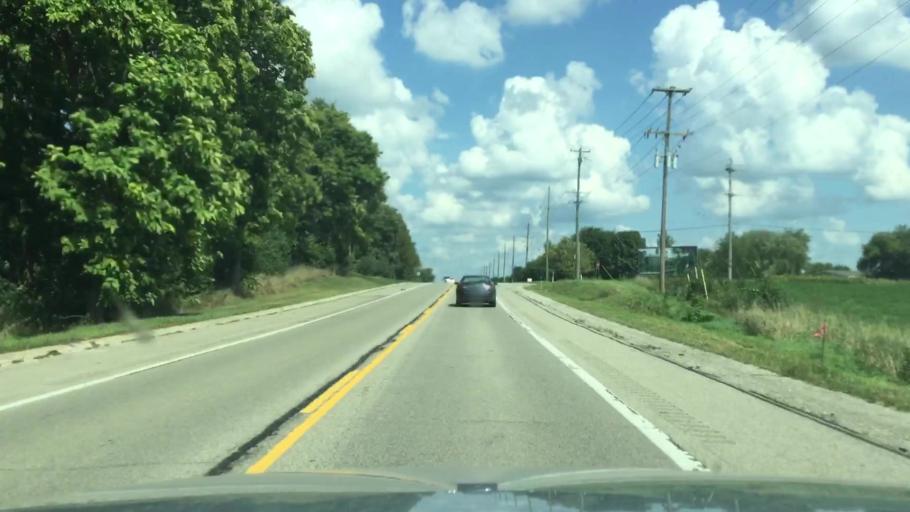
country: US
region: Michigan
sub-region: Washtenaw County
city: Saline
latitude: 42.1561
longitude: -83.8072
